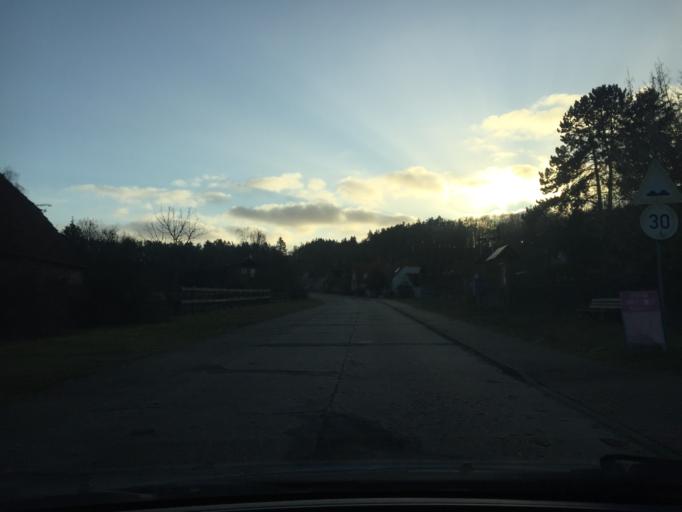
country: DE
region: Lower Saxony
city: Hitzacker
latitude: 53.1800
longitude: 10.9843
